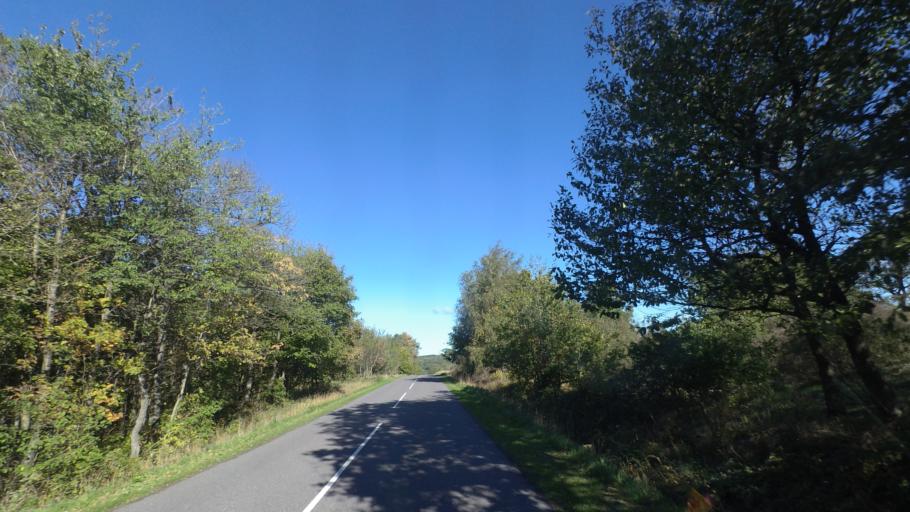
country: DK
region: Capital Region
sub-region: Bornholm Kommune
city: Nexo
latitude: 55.0710
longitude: 15.0821
